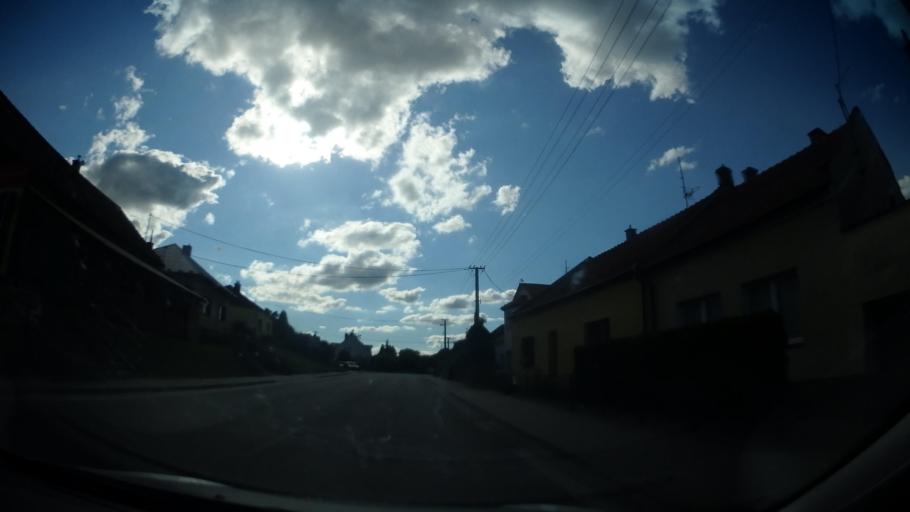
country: CZ
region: South Moravian
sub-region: Okres Blansko
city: Rajec-Jestrebi
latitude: 49.4098
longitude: 16.6208
